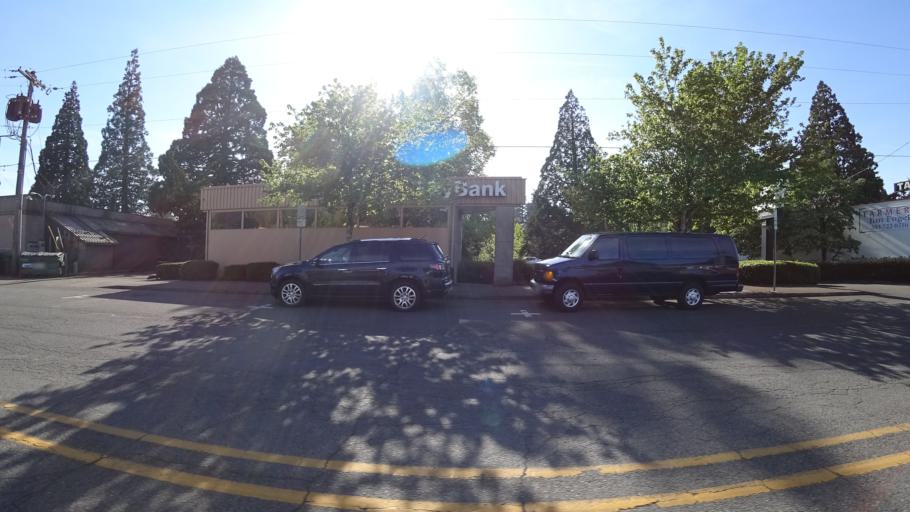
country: US
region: Oregon
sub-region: Clackamas County
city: Milwaukie
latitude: 45.4474
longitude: -122.6420
